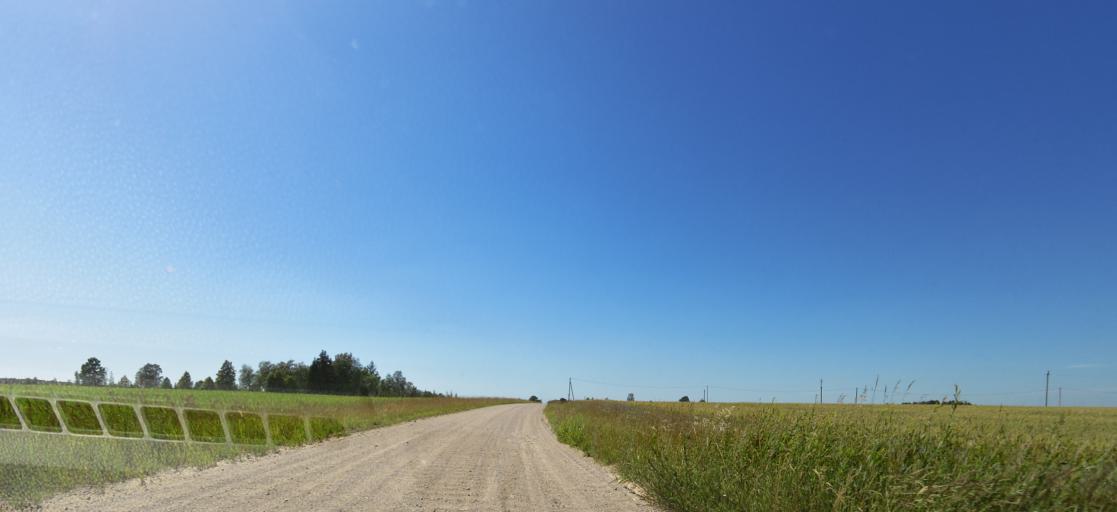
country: LT
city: Vabalninkas
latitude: 55.9347
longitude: 24.6693
